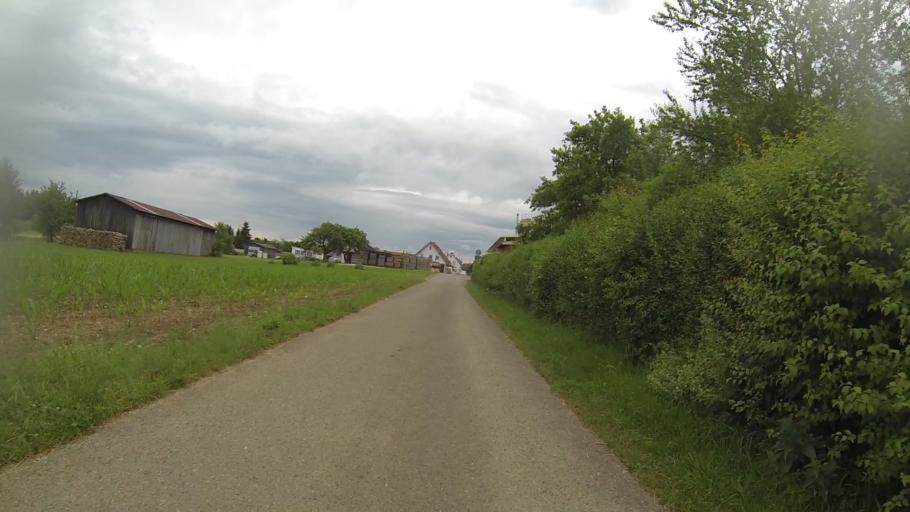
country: DE
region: Baden-Wuerttemberg
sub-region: Tuebingen Region
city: Blaubeuren
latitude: 48.4409
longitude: 9.8244
